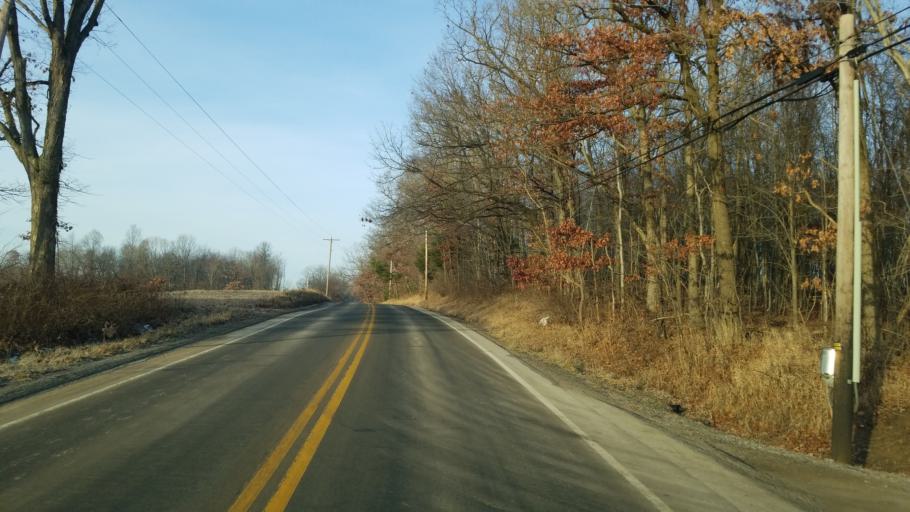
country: US
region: Pennsylvania
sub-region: Indiana County
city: Chevy Chase Heights
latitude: 40.8711
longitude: -79.2292
